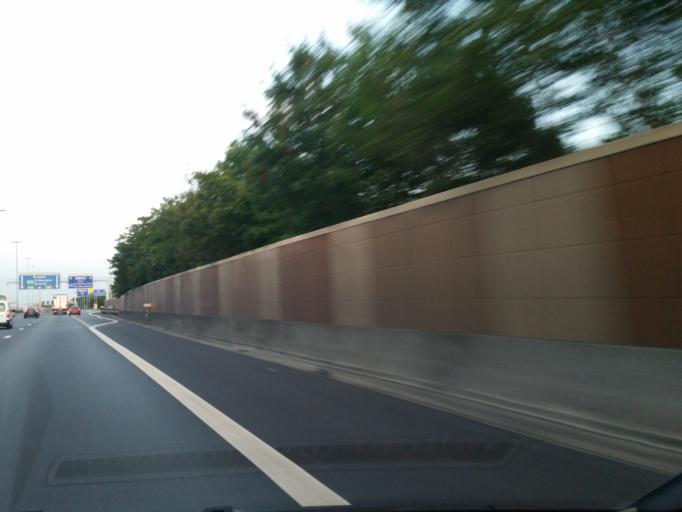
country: BE
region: Flanders
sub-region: Provincie Oost-Vlaanderen
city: Sint-Martens-Latem
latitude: 51.0229
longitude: 3.6779
